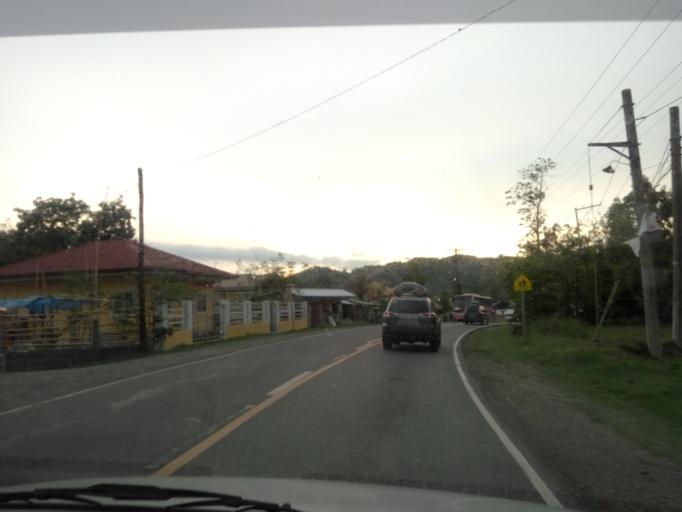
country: PH
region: Ilocos
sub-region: Province of La Union
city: Damortis
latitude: 16.2350
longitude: 120.4325
